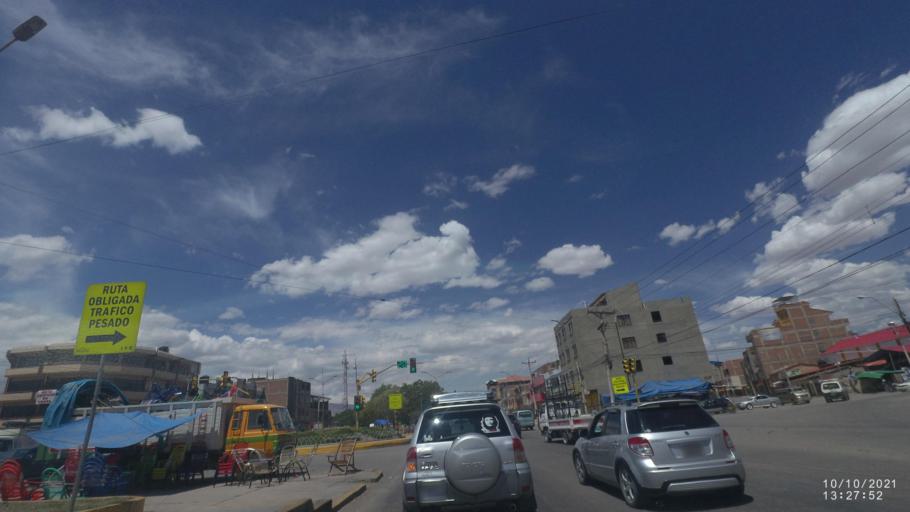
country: BO
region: Cochabamba
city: Sipe Sipe
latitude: -17.3945
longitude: -66.2867
